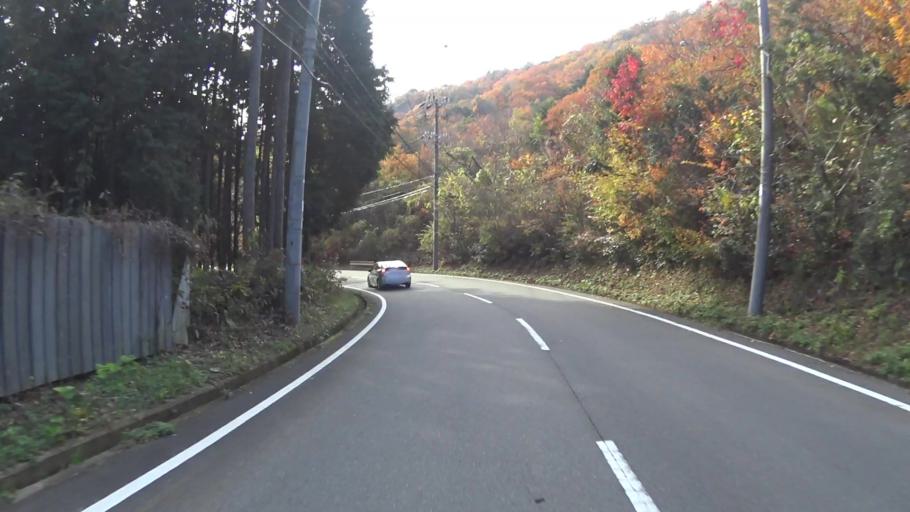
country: JP
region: Kyoto
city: Maizuru
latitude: 35.5308
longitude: 135.3934
